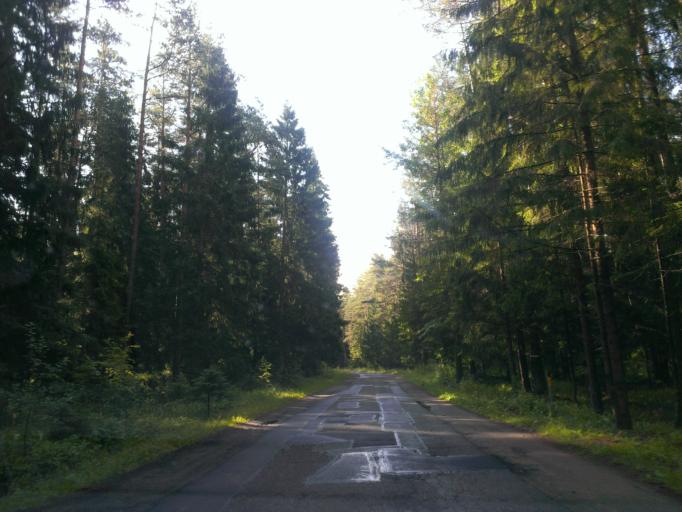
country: LV
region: Incukalns
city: Vangazi
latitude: 57.0978
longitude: 24.5342
